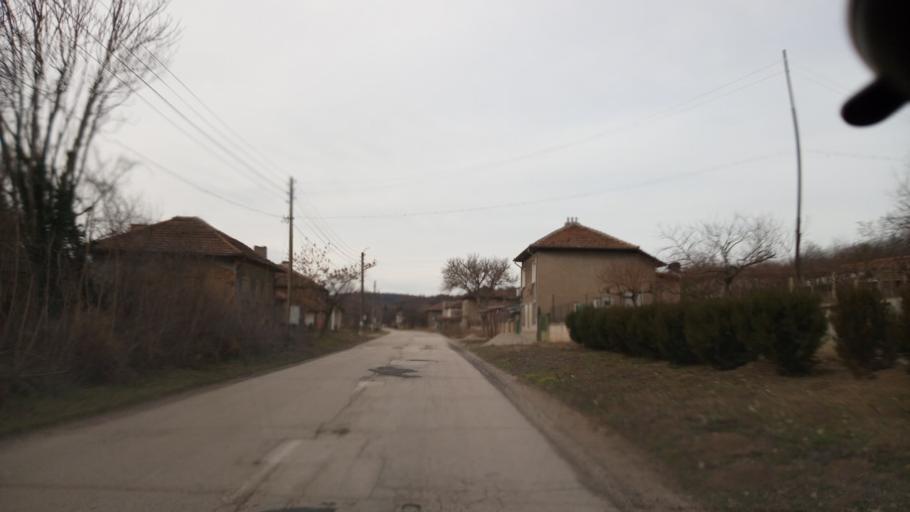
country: BG
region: Pleven
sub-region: Obshtina Belene
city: Belene
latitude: 43.6101
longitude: 25.0117
